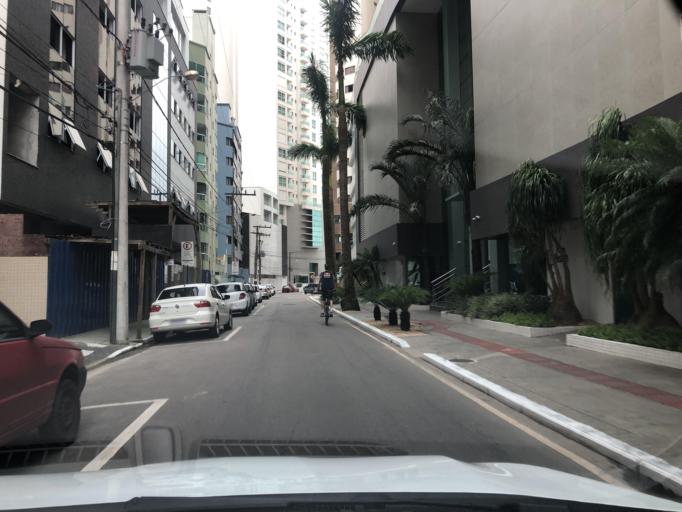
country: BR
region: Santa Catarina
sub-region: Balneario Camboriu
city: Balneario Camboriu
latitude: -27.0011
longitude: -48.6229
